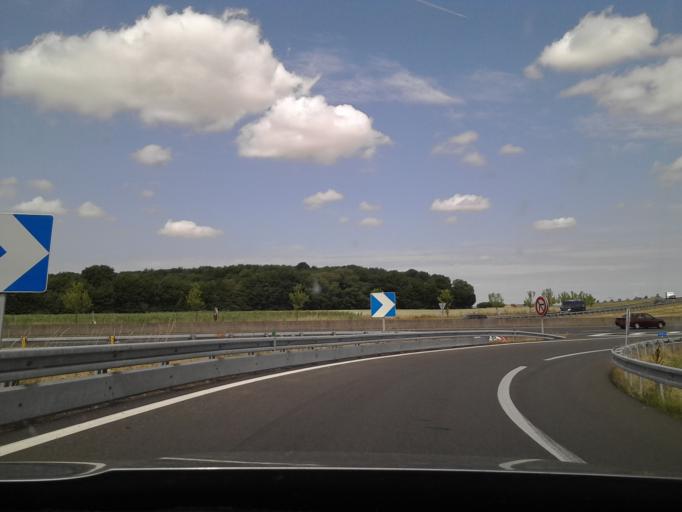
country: FR
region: Centre
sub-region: Departement d'Indre-et-Loire
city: Parcay-Meslay
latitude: 47.4638
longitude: 0.7632
